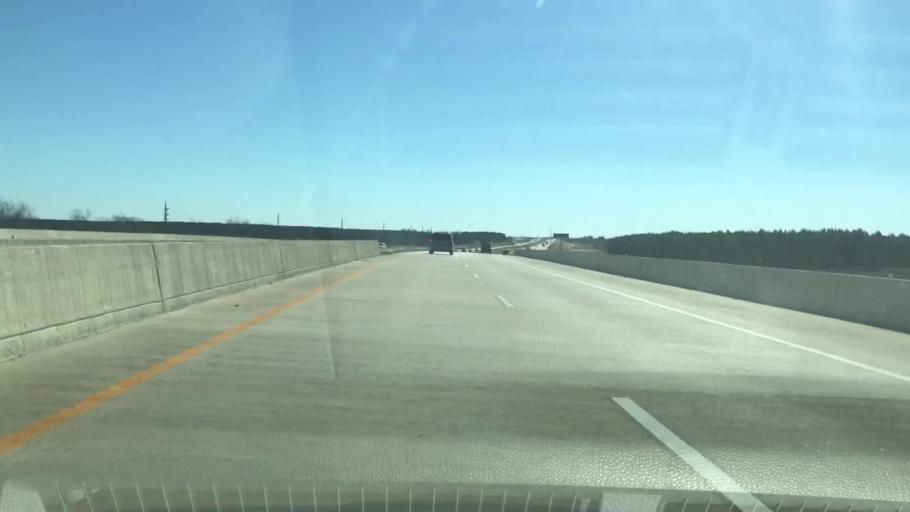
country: US
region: Texas
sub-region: Harris County
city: Cypress
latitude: 29.9041
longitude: -95.7586
